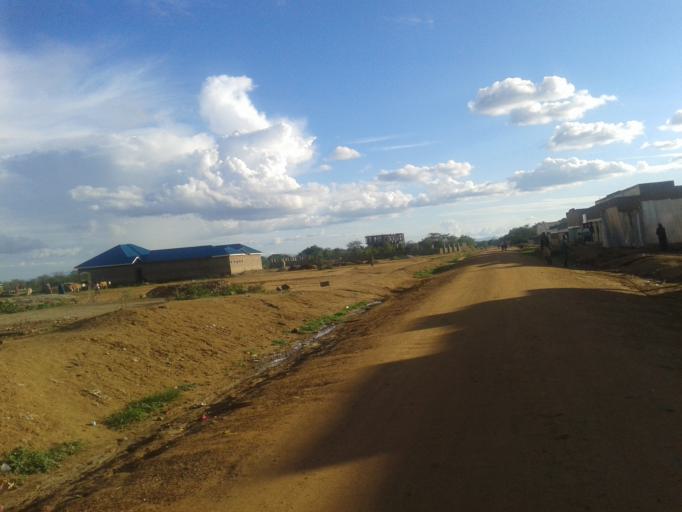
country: UG
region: Northern Region
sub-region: Kotido District
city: Kotido
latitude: 3.0042
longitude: 34.1131
